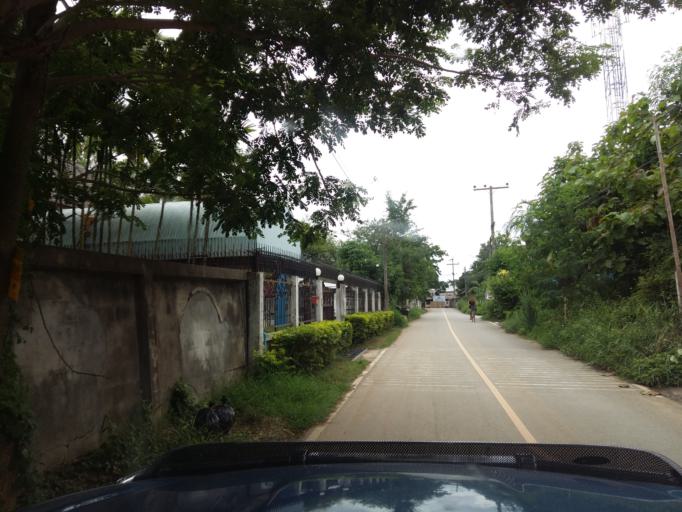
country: TH
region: Chiang Mai
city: San Sai
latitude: 18.7862
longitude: 99.0542
